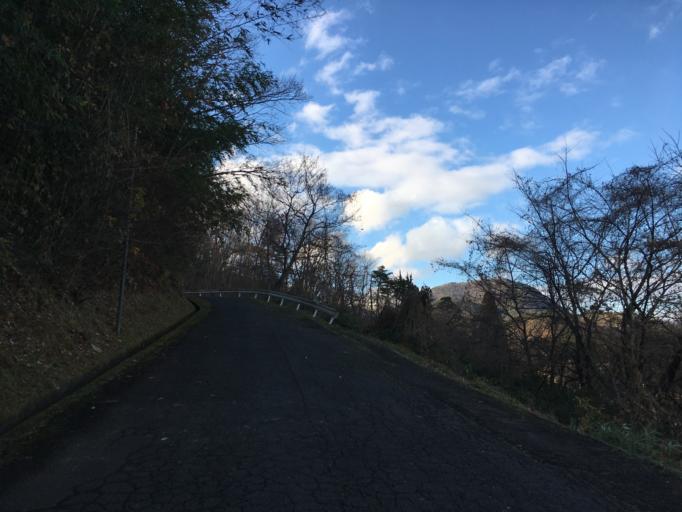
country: JP
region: Fukushima
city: Fukushima-shi
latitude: 37.8327
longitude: 140.4405
